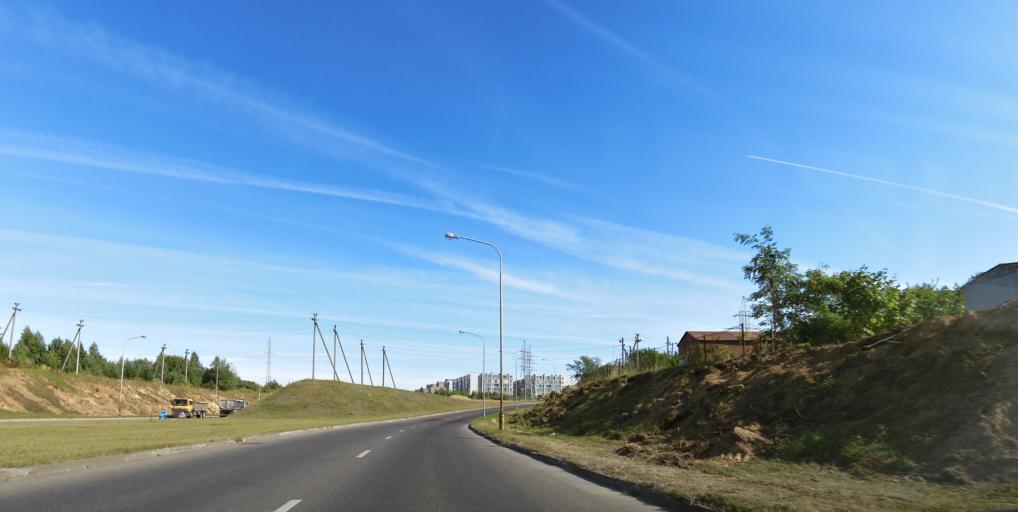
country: LT
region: Vilnius County
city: Justiniskes
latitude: 54.7043
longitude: 25.2100
